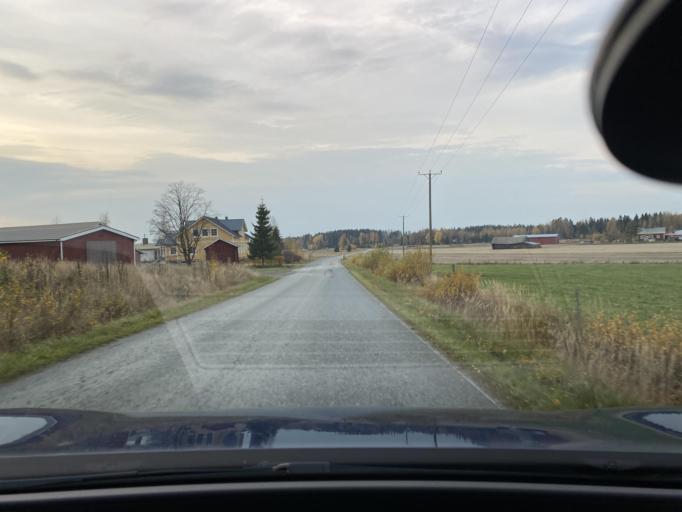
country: FI
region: Pirkanmaa
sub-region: Lounais-Pirkanmaa
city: Punkalaidun
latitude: 61.0763
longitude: 22.9639
